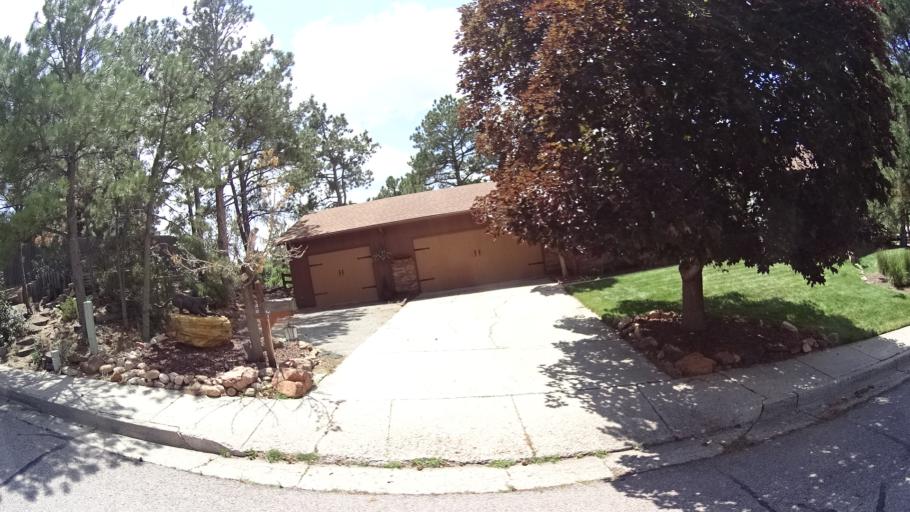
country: US
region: Colorado
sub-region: El Paso County
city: Air Force Academy
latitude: 38.9340
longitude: -104.8283
